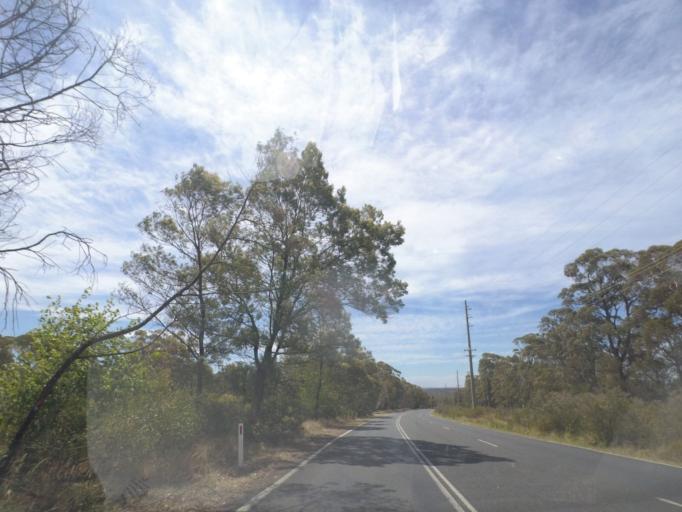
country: AU
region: New South Wales
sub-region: Wingecarribee
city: Colo Vale
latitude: -34.4003
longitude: 150.5316
